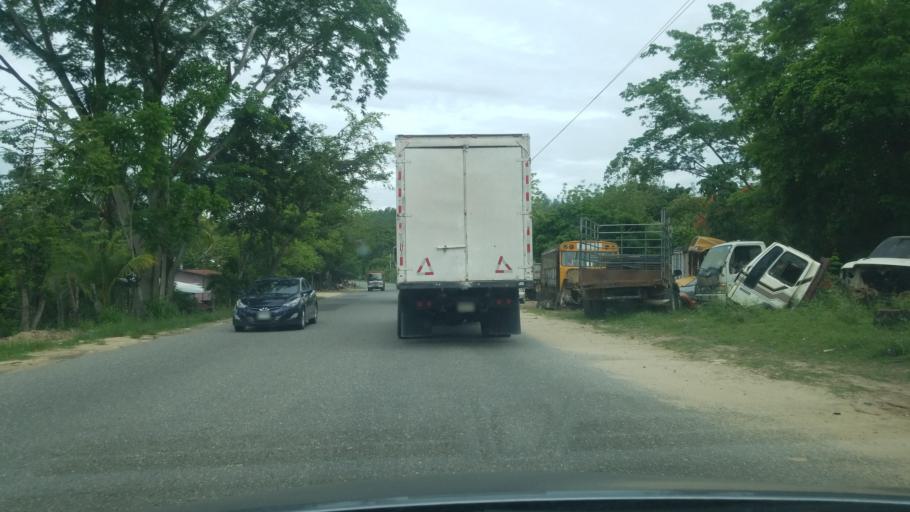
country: HN
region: Santa Barbara
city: San Marcos
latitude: 15.3137
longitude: -88.4361
